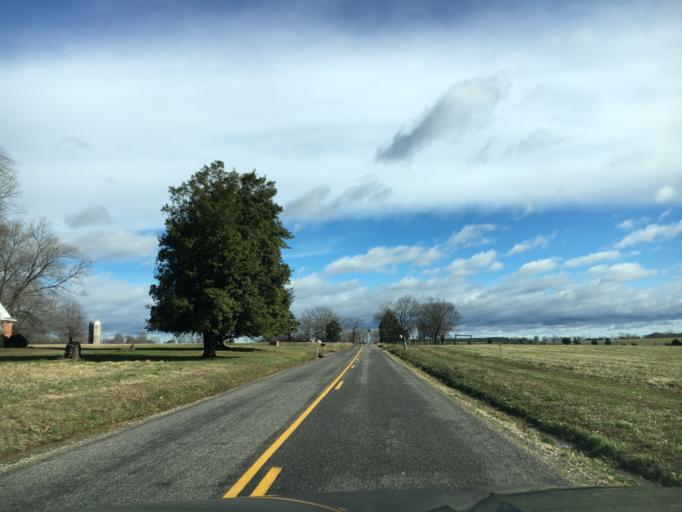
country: US
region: Virginia
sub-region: Amelia County
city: Amelia Court House
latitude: 37.4485
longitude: -77.9805
